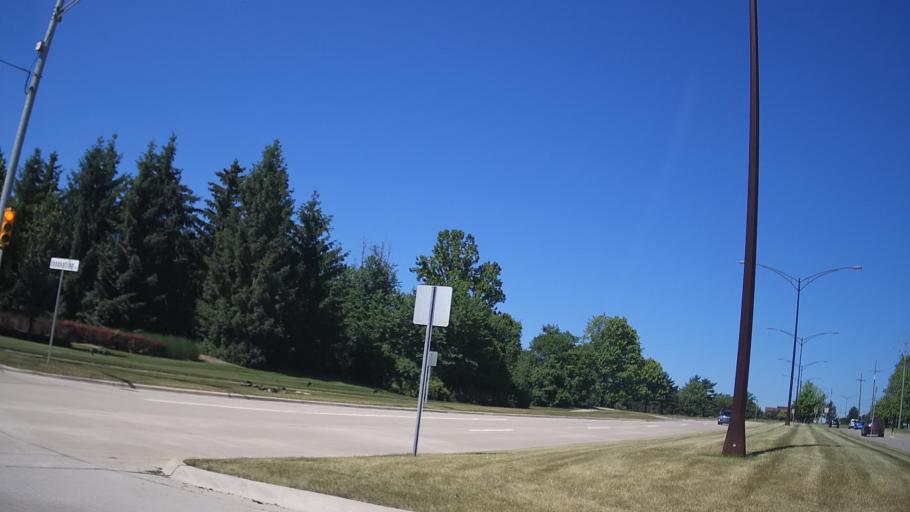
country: US
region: Michigan
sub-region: Oakland County
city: Troy
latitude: 42.6060
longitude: -83.1629
